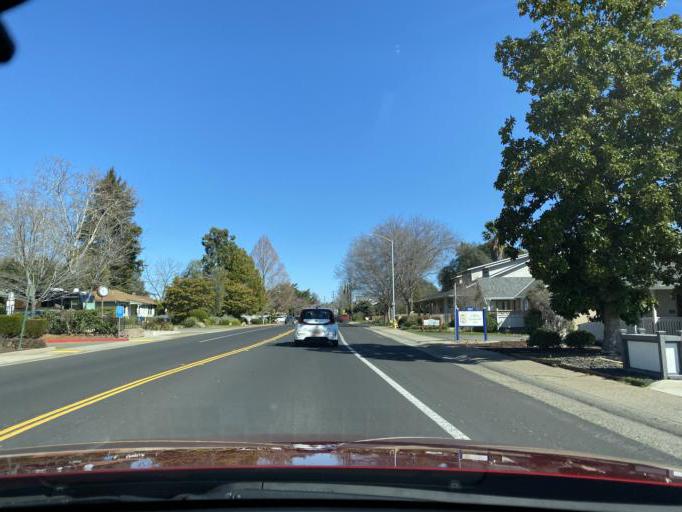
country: US
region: California
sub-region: Sacramento County
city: Folsom
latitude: 38.6779
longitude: -121.1697
